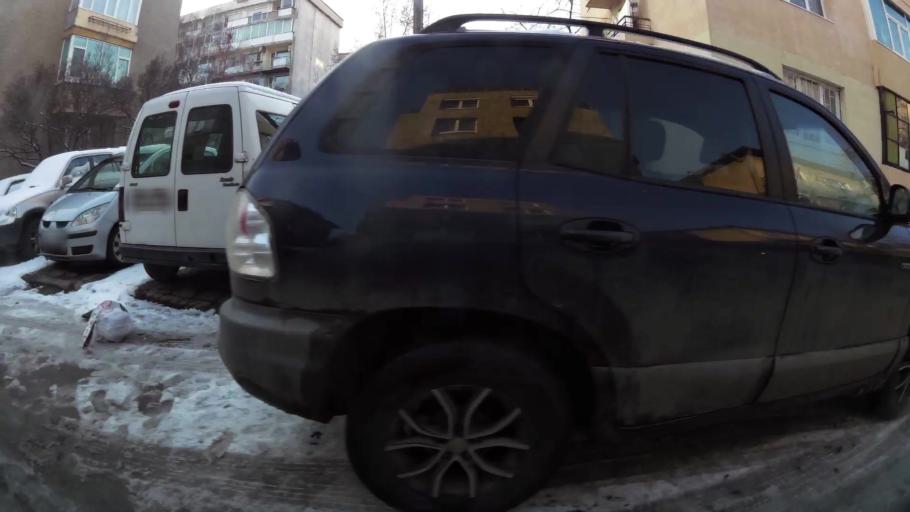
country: BG
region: Sofia-Capital
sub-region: Stolichna Obshtina
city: Sofia
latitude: 42.6800
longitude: 23.3641
